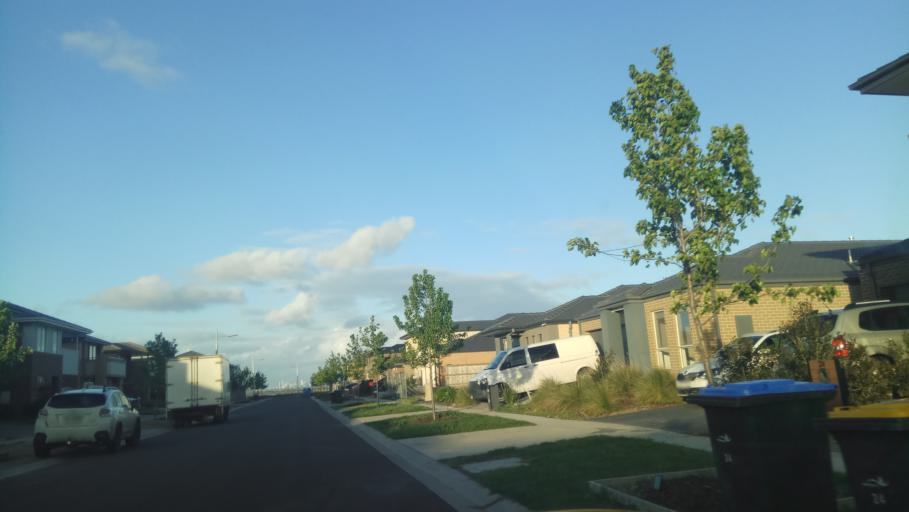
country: AU
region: Victoria
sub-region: Hobsons Bay
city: Altona Meadows
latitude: -37.9112
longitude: 144.7801
